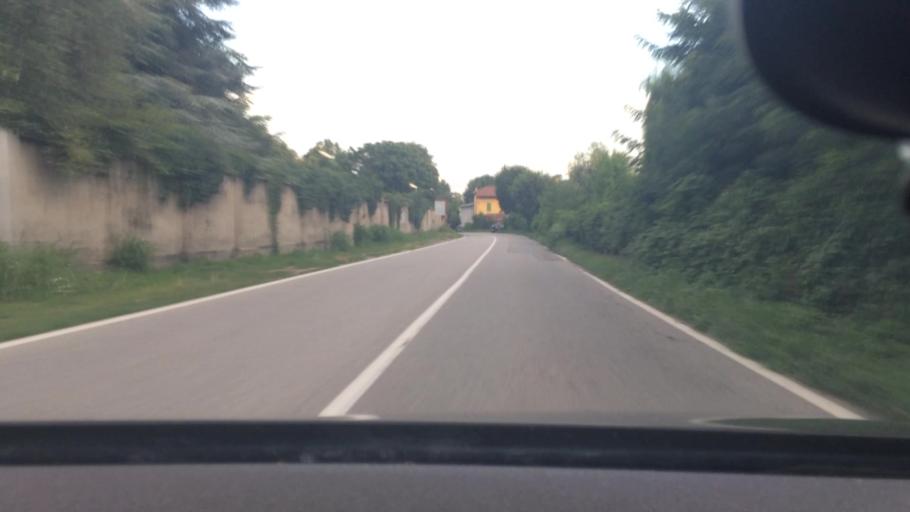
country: IT
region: Lombardy
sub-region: Citta metropolitana di Milano
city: Pregnana Milanese
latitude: 45.5226
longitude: 9.0263
